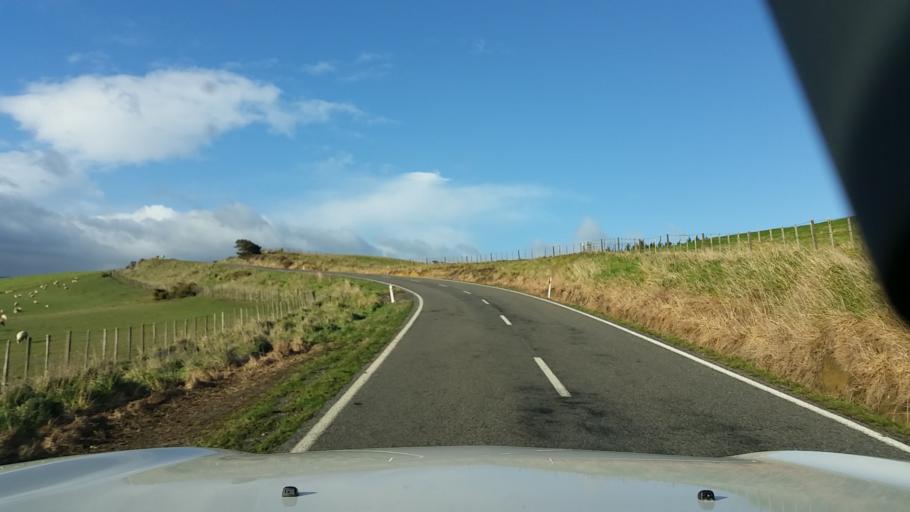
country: NZ
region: Wellington
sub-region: Upper Hutt City
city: Upper Hutt
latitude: -41.3753
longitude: 175.1782
